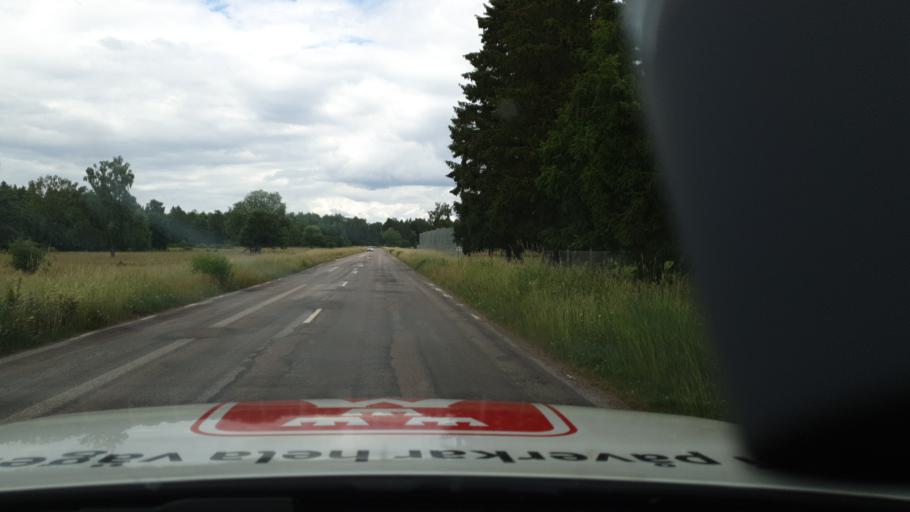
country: SE
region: Vaestra Goetaland
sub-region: Skara Kommun
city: Axvall
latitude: 58.3942
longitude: 13.5783
